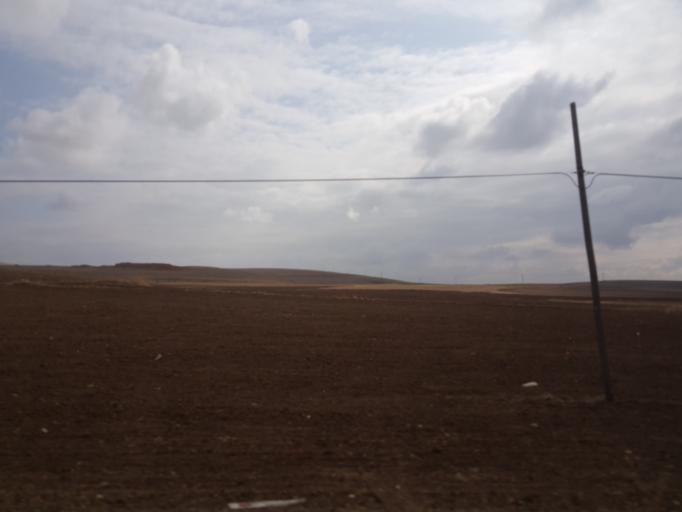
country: TR
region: Kirikkale
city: Keskin
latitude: 39.5806
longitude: 33.5945
